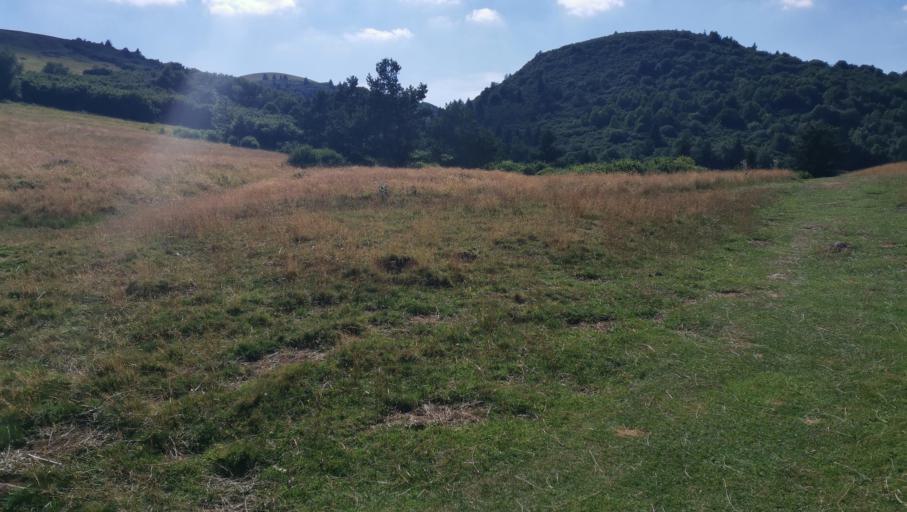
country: FR
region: Auvergne
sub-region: Departement du Puy-de-Dome
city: Orcines
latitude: 45.7932
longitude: 2.9687
